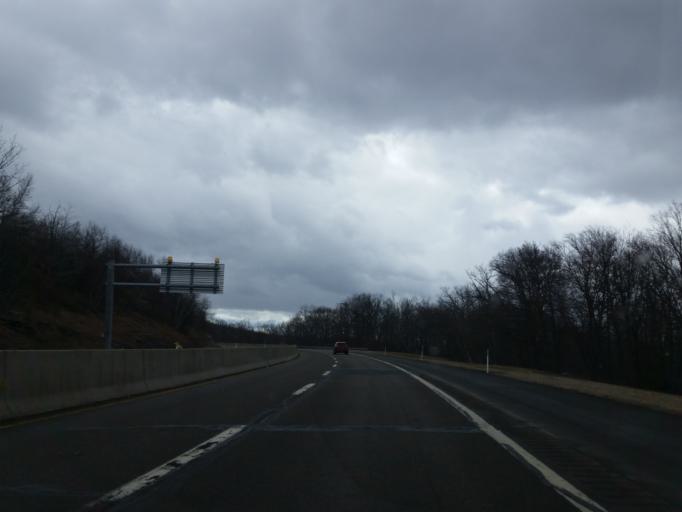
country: US
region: Pennsylvania
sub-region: Luzerne County
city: Laflin
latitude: 41.2697
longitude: -75.7773
